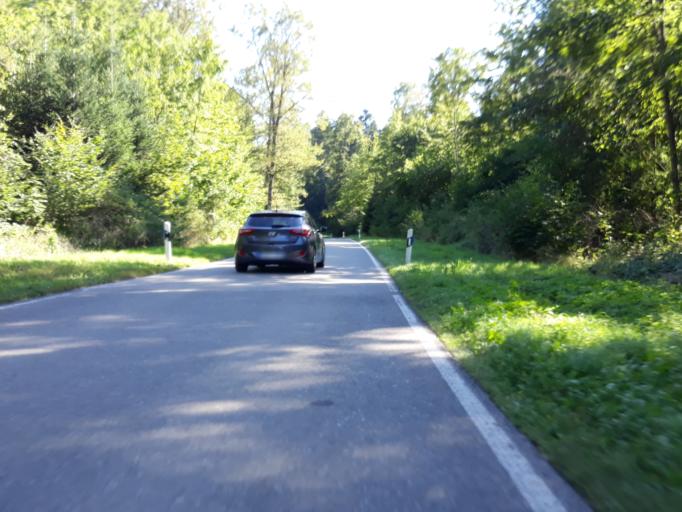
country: DE
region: Baden-Wuerttemberg
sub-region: Karlsruhe Region
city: Ostelsheim
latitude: 48.7143
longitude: 8.8424
